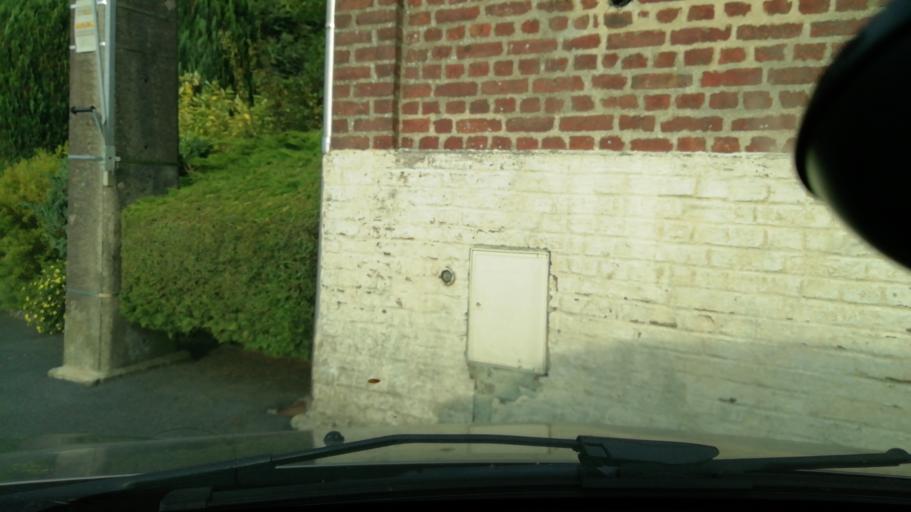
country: FR
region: Nord-Pas-de-Calais
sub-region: Departement du Nord
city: Caudry
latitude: 50.1210
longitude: 3.4403
